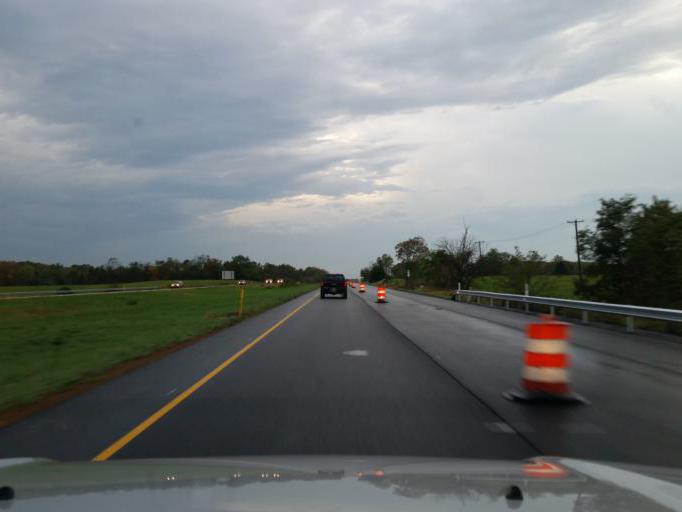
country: US
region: Pennsylvania
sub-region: Adams County
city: Lake Heritage
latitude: 39.7842
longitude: -77.2201
